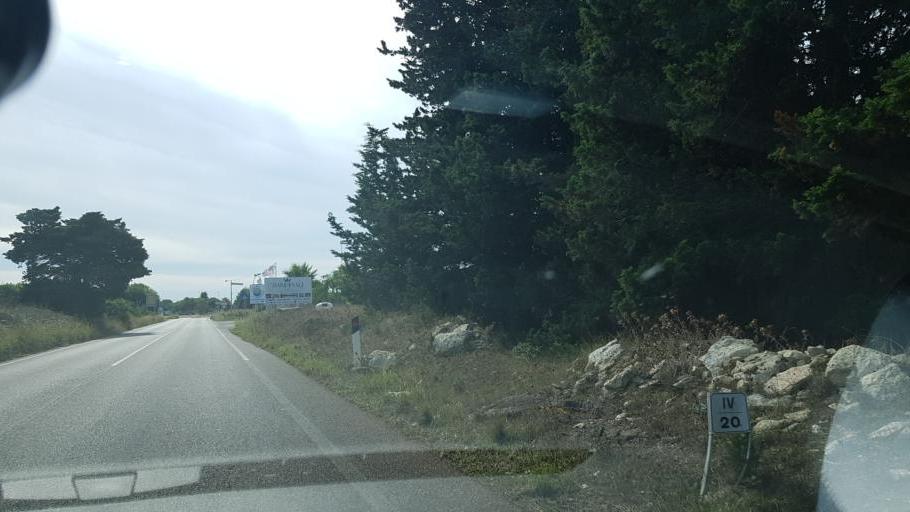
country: IT
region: Apulia
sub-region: Provincia di Lecce
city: Borgagne
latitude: 40.2562
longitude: 18.4372
